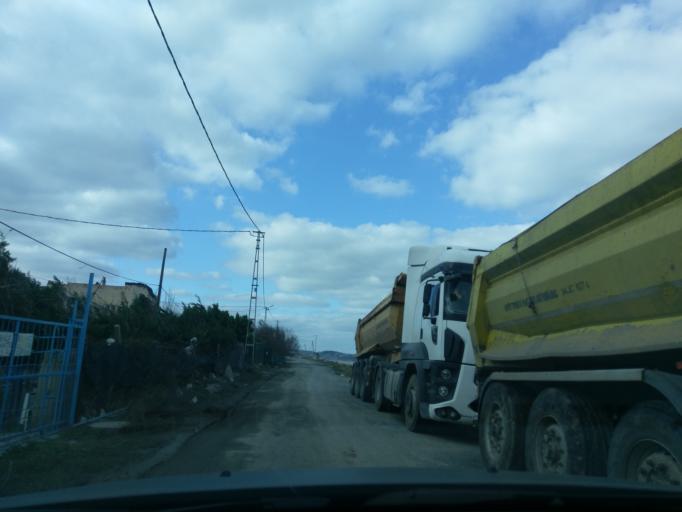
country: TR
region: Istanbul
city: Durusu
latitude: 41.3238
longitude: 28.7303
